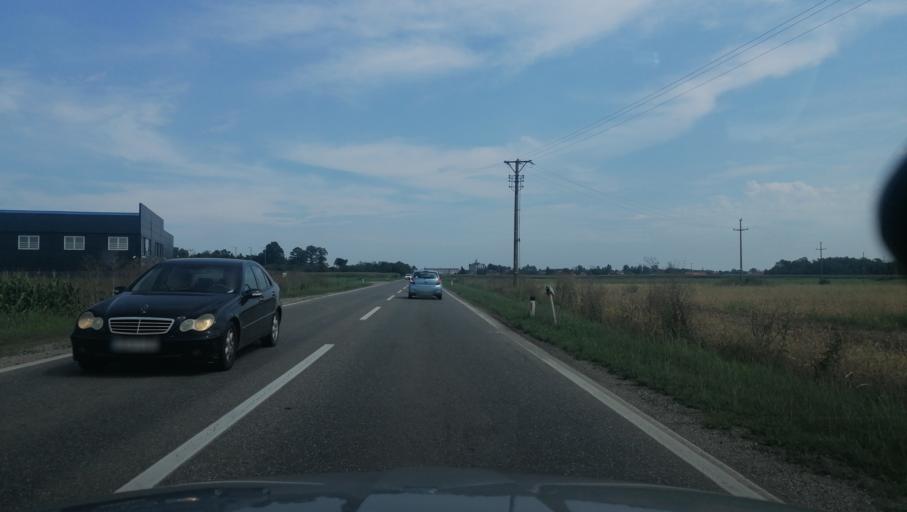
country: BA
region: Republika Srpska
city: Dvorovi
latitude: 44.7874
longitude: 19.2603
